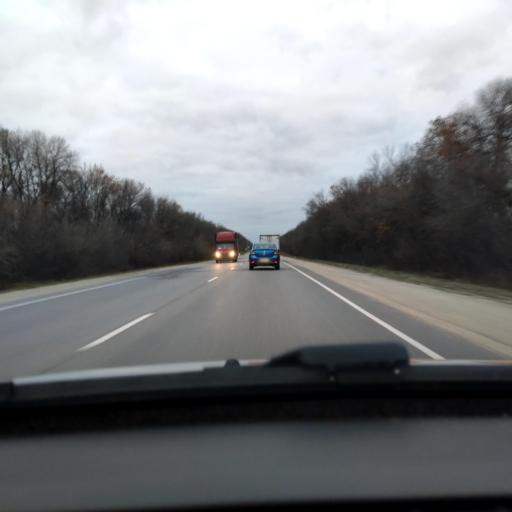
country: RU
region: Lipetsk
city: Borinskoye
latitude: 52.3864
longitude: 39.2244
